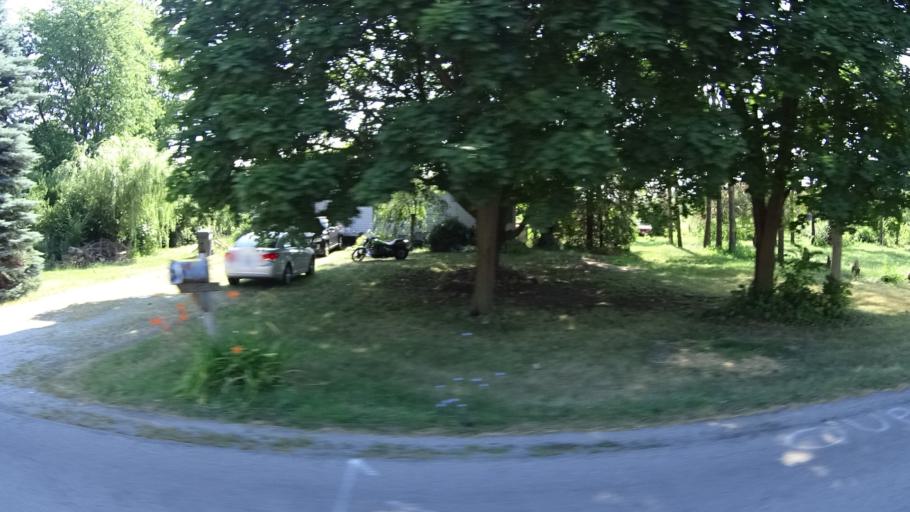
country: US
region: Ohio
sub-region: Huron County
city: Bellevue
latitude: 41.3738
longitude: -82.7951
